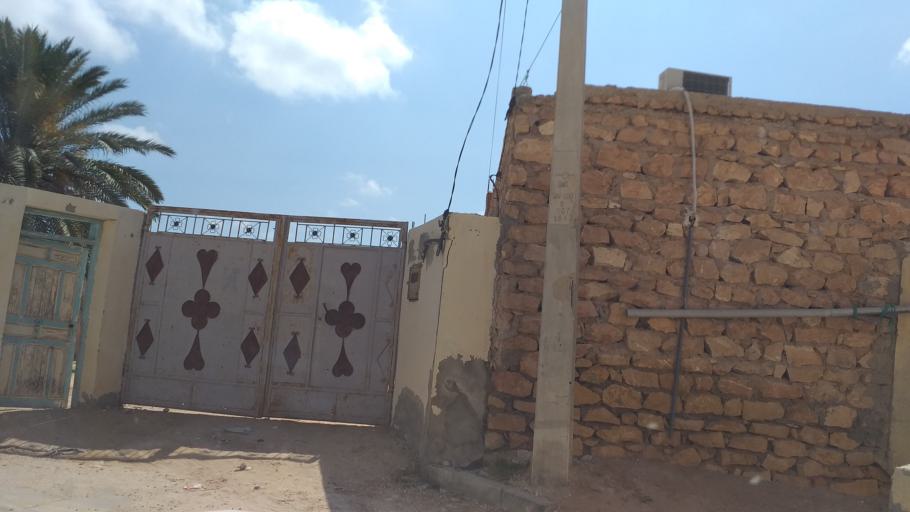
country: TN
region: Qabis
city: Gabes
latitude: 33.9432
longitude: 10.0663
